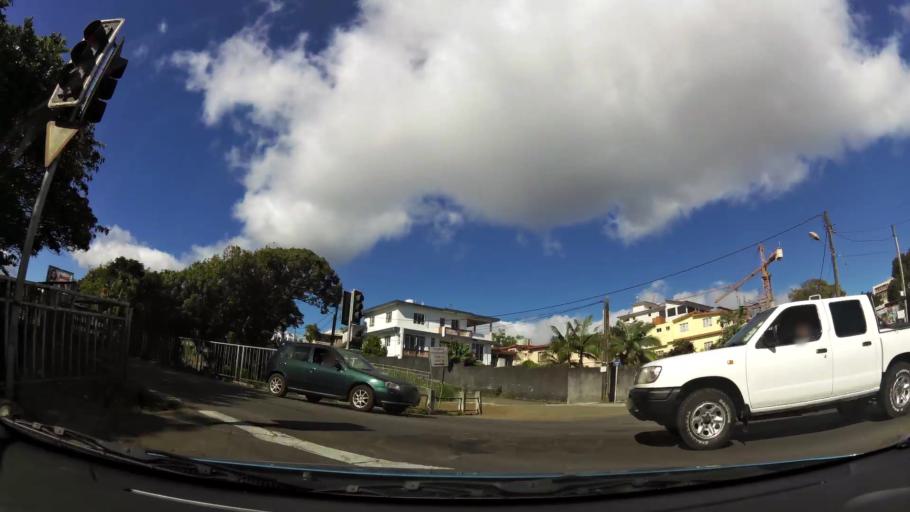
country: MU
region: Plaines Wilhems
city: Curepipe
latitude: -20.3081
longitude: 57.5140
